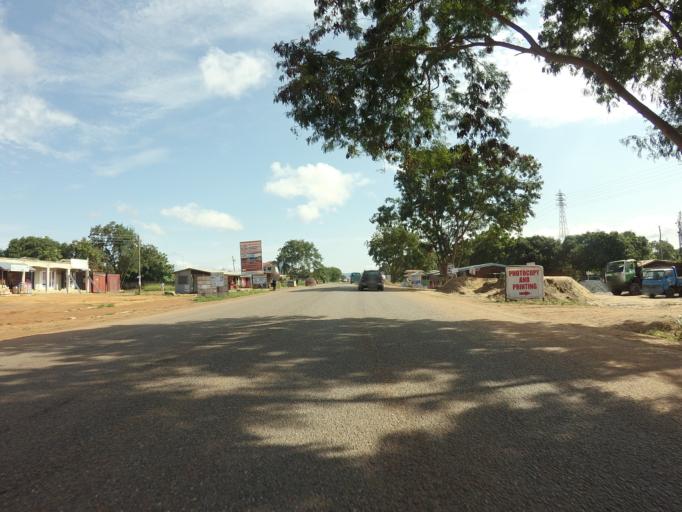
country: GH
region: Eastern
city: Aburi
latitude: 5.7965
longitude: -0.1281
